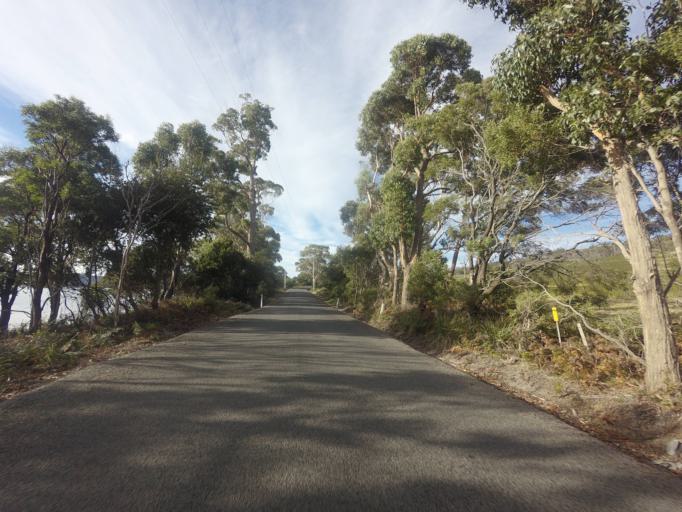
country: AU
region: Tasmania
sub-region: Sorell
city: Sorell
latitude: -42.9649
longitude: 147.8318
